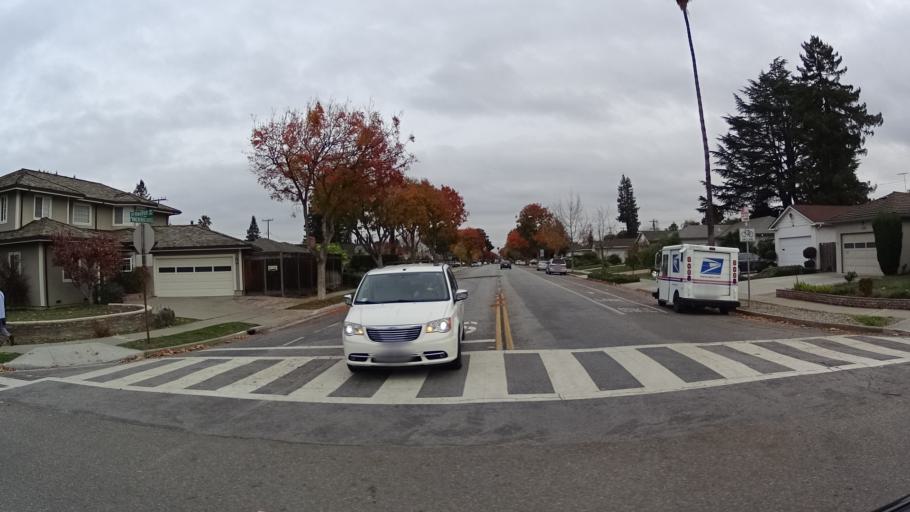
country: US
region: California
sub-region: Santa Clara County
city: Sunnyvale
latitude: 37.3643
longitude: -122.0589
